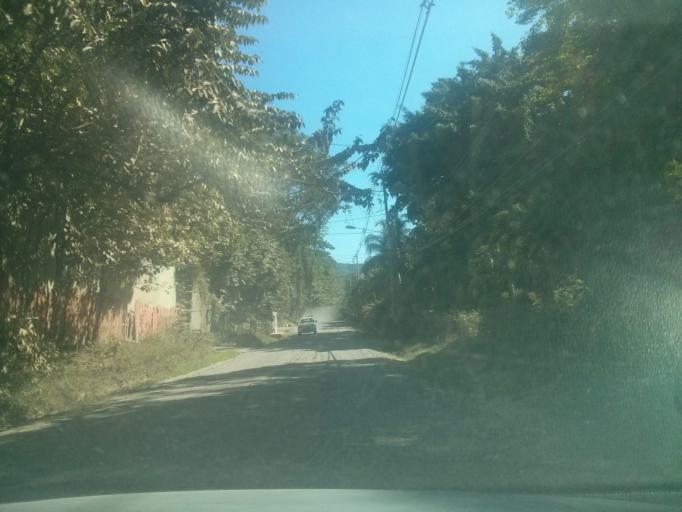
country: CR
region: Puntarenas
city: Paquera
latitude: 9.6184
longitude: -85.1443
